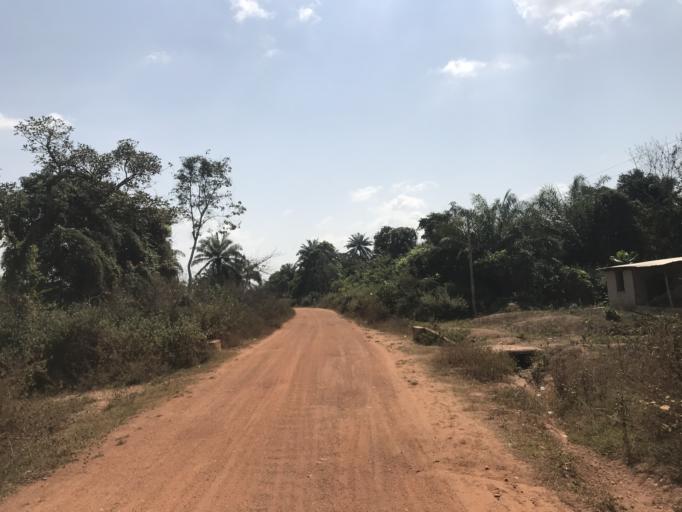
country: NG
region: Osun
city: Ifon
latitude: 7.8779
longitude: 4.4784
